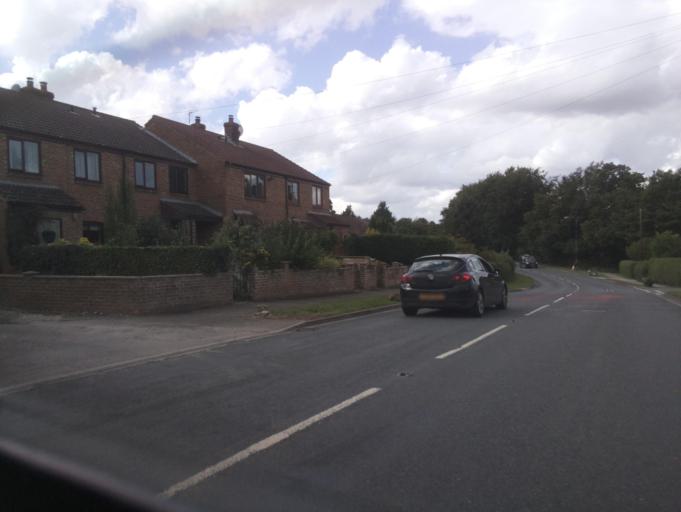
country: GB
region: England
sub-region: North Yorkshire
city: Ripon
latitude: 54.1894
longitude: -1.5626
